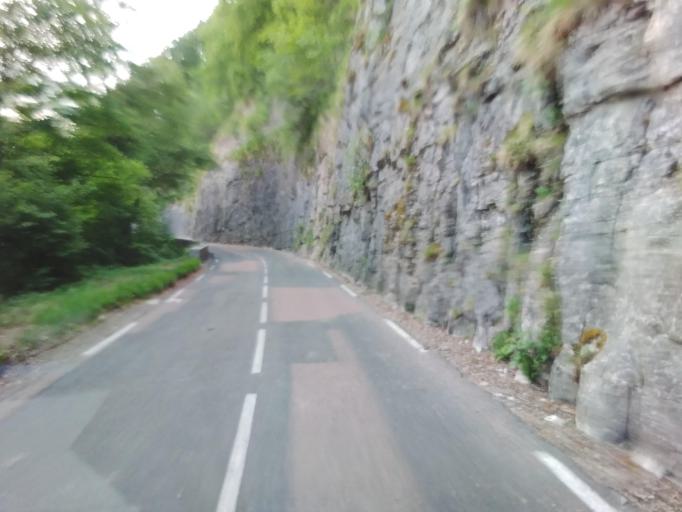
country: FR
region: Franche-Comte
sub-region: Departement du Jura
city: Arbois
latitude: 46.8714
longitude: 5.7994
